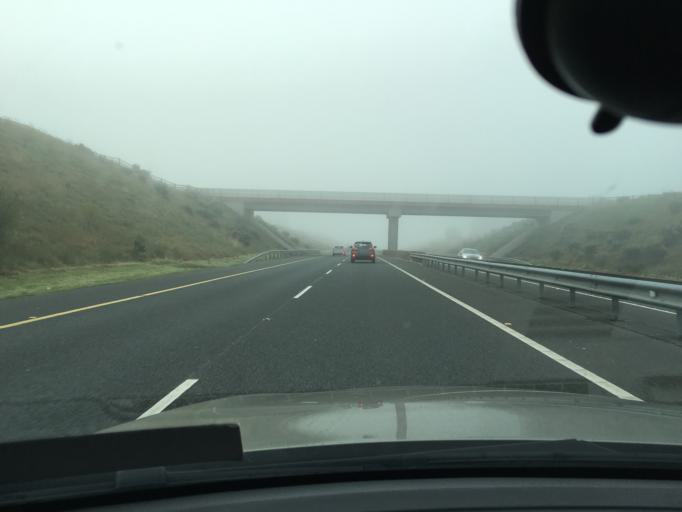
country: IE
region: Leinster
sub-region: An Iarmhi
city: Athlone
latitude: 53.3835
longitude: -8.0507
